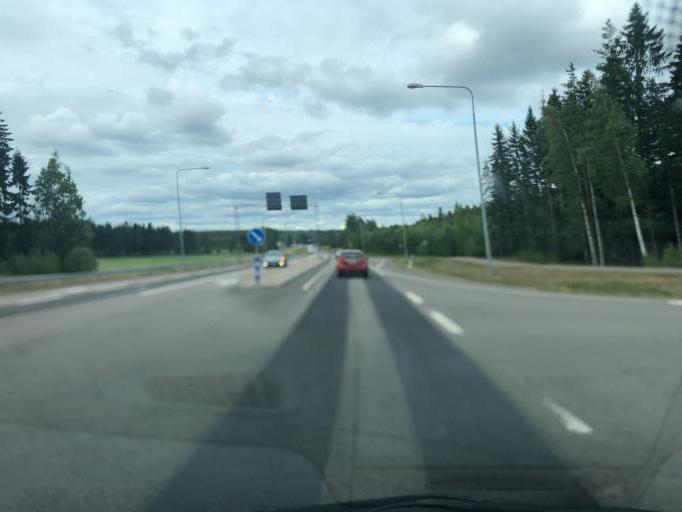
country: FI
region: Kymenlaakso
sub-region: Kouvola
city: Kouvola
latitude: 60.9215
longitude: 26.7891
